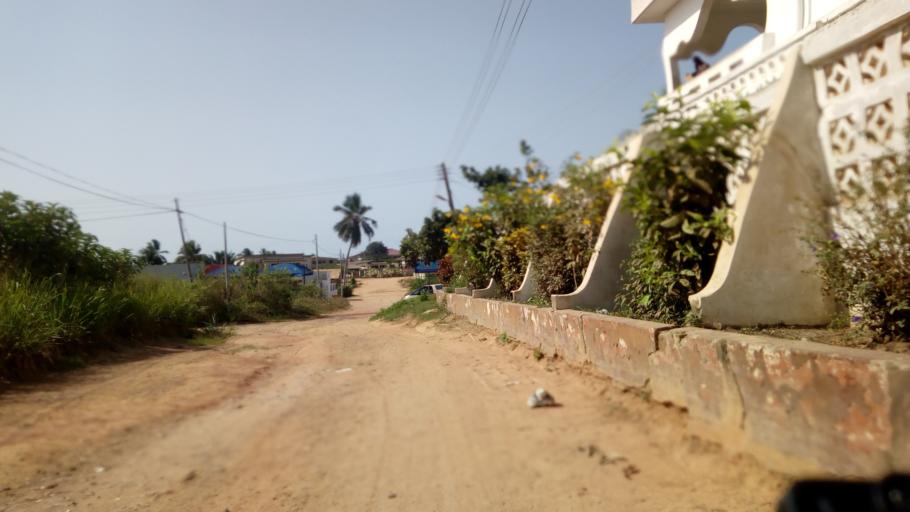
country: GH
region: Central
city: Cape Coast
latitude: 5.1200
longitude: -1.2706
